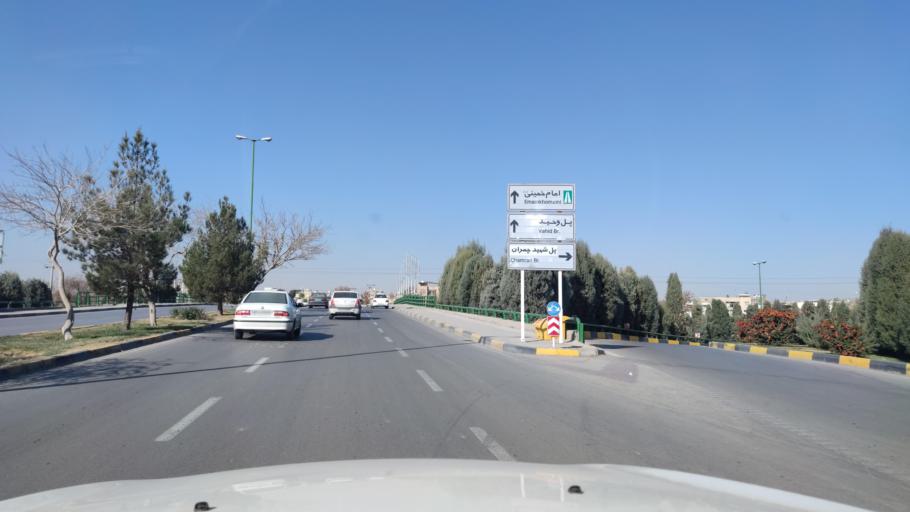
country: IR
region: Isfahan
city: Isfahan
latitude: 32.6824
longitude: 51.6469
